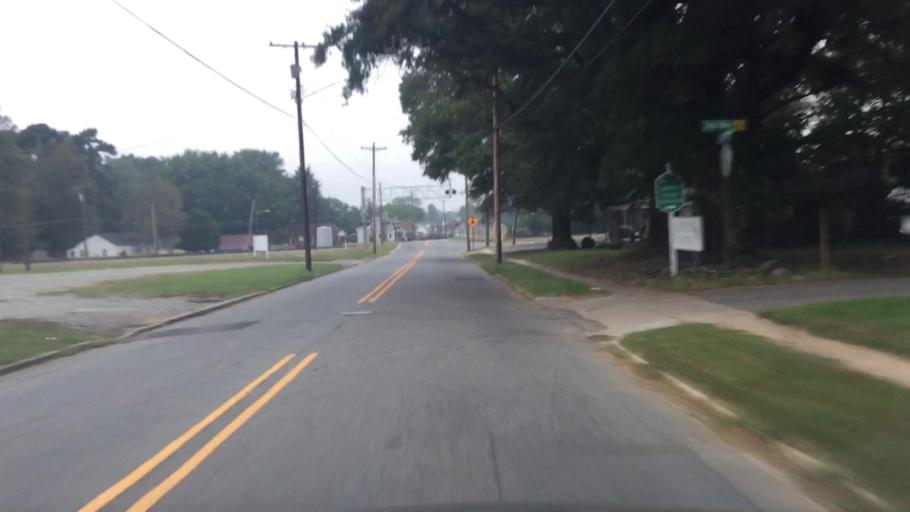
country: US
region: North Carolina
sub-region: Iredell County
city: Mooresville
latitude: 35.5937
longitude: -80.8067
